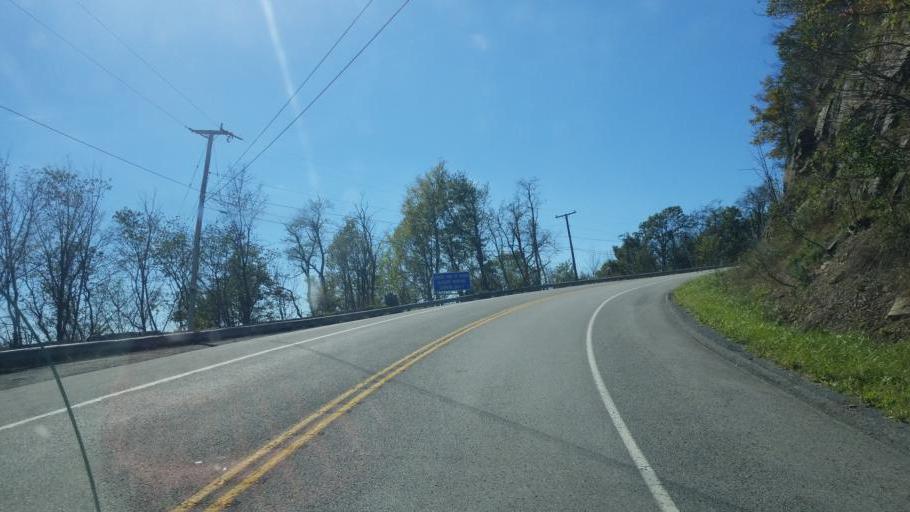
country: US
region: Pennsylvania
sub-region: Somerset County
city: Central City
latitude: 40.0376
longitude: -78.7586
